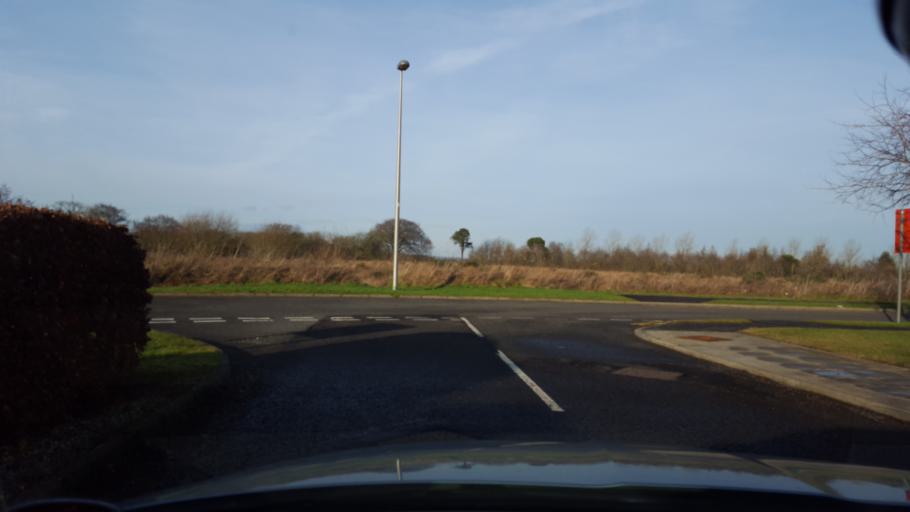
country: GB
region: Scotland
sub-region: West Lothian
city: West Calder
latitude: 55.8735
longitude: -3.5494
